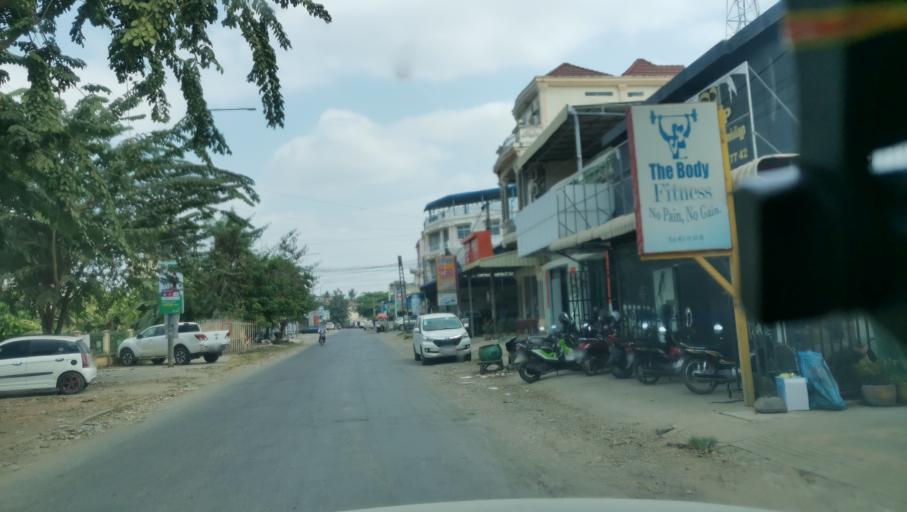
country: KH
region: Battambang
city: Battambang
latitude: 13.0864
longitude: 103.1991
